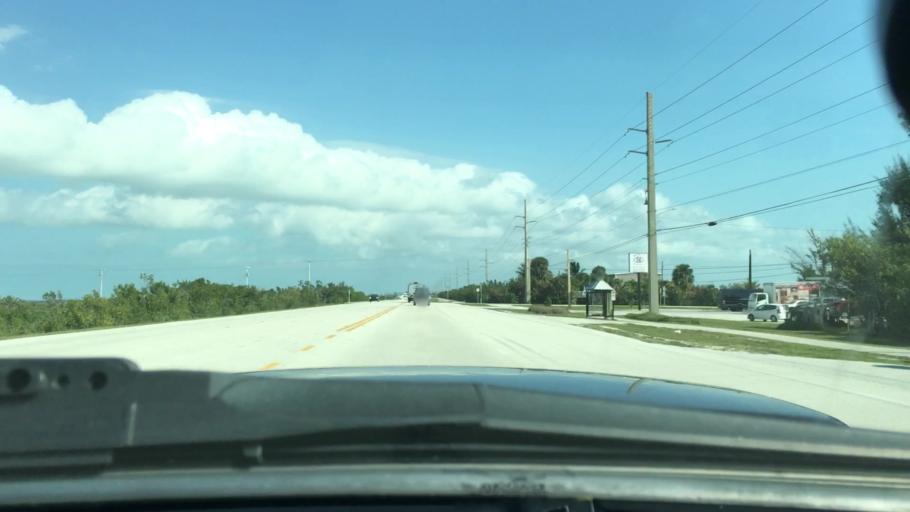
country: US
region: Florida
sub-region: Monroe County
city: Big Coppitt Key
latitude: 24.6286
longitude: -81.5938
